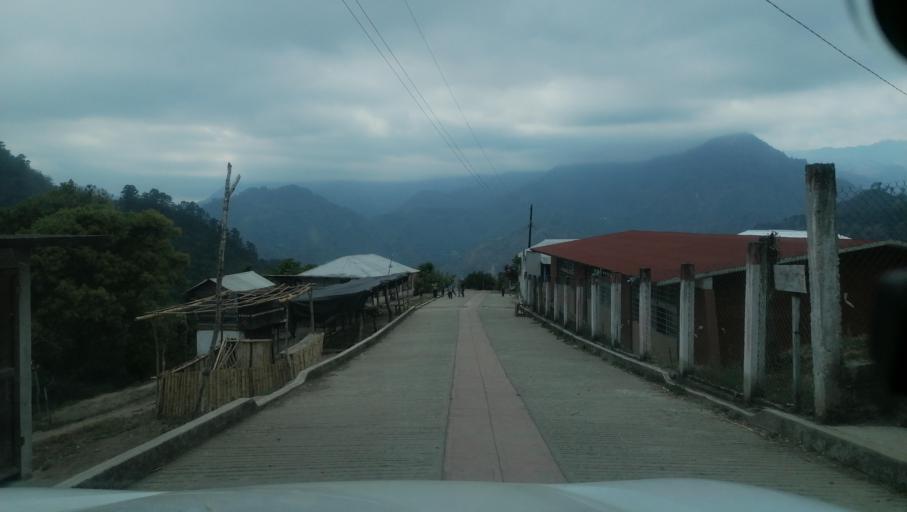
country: GT
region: San Marcos
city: Sibinal
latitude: 15.1646
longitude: -92.1552
